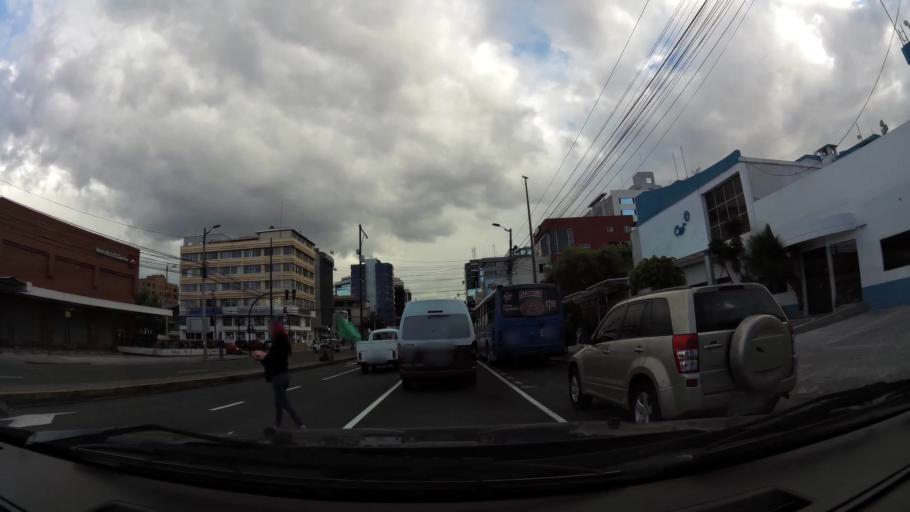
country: EC
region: Pichincha
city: Quito
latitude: -0.1688
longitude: -78.4844
